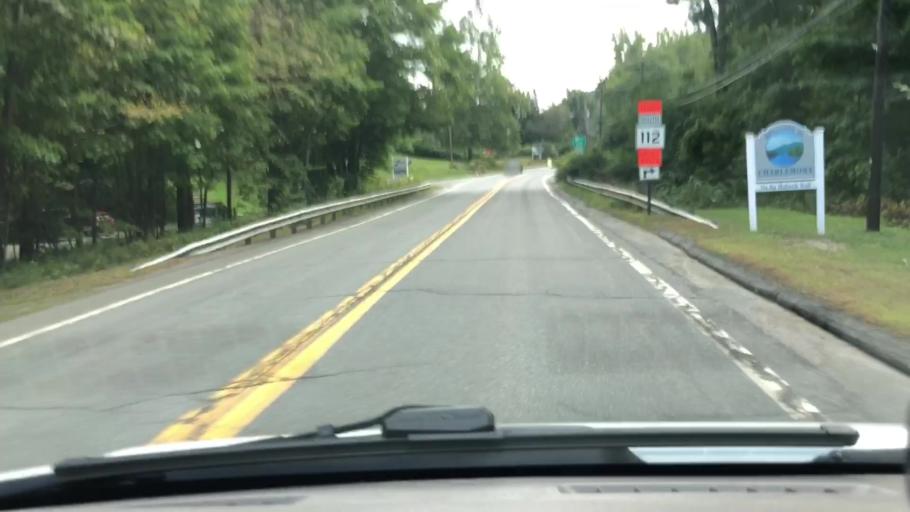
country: US
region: Massachusetts
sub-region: Franklin County
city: Charlemont
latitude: 42.6277
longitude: -72.8849
